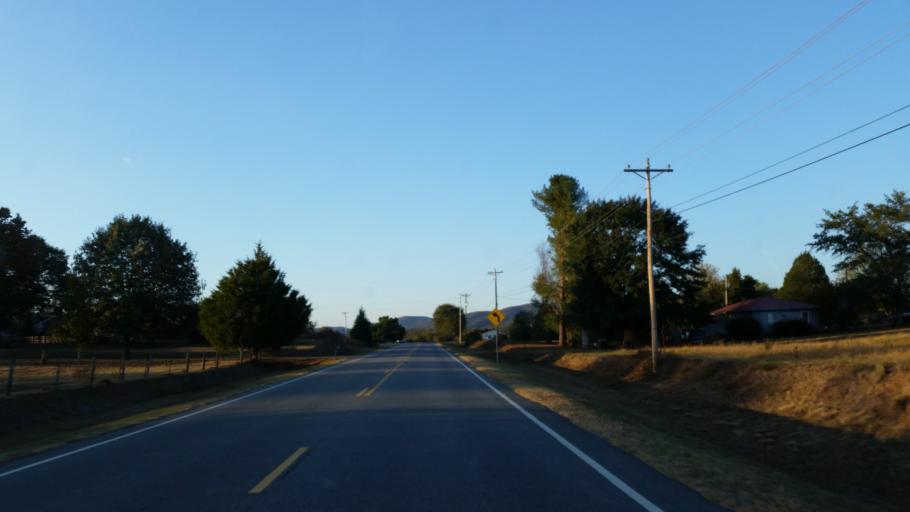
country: US
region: Georgia
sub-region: Gordon County
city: Calhoun
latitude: 34.5763
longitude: -85.0258
